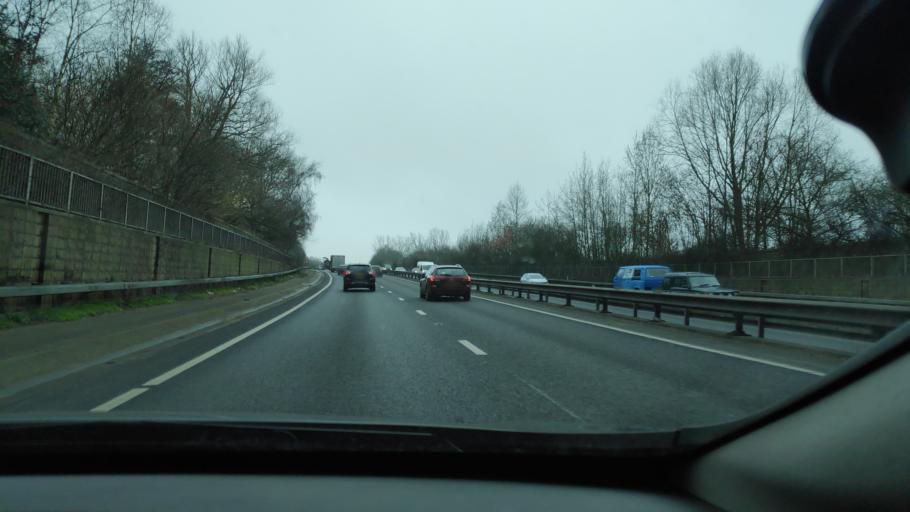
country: GB
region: England
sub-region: Hampshire
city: Aldershot
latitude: 51.2594
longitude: -0.7336
